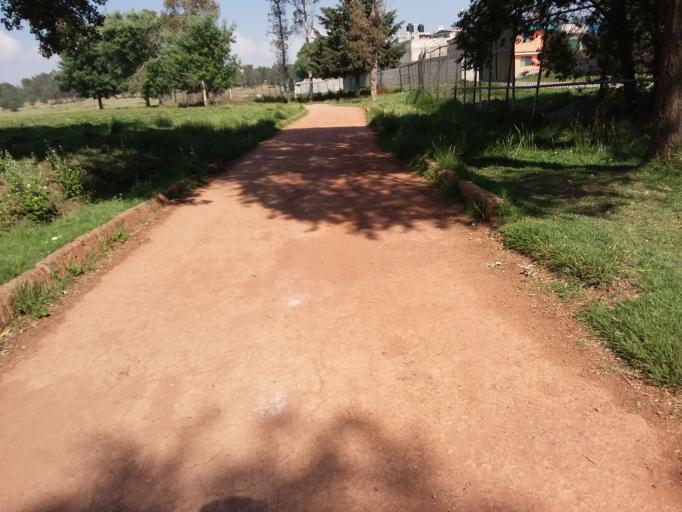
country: MX
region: Mexico
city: San Buenaventura
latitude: 19.2774
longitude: -99.6920
